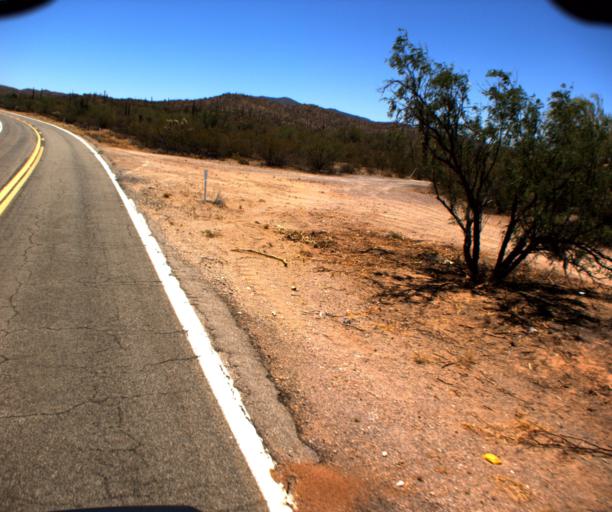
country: US
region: Arizona
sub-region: Pima County
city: Sells
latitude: 32.1751
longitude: -112.2281
